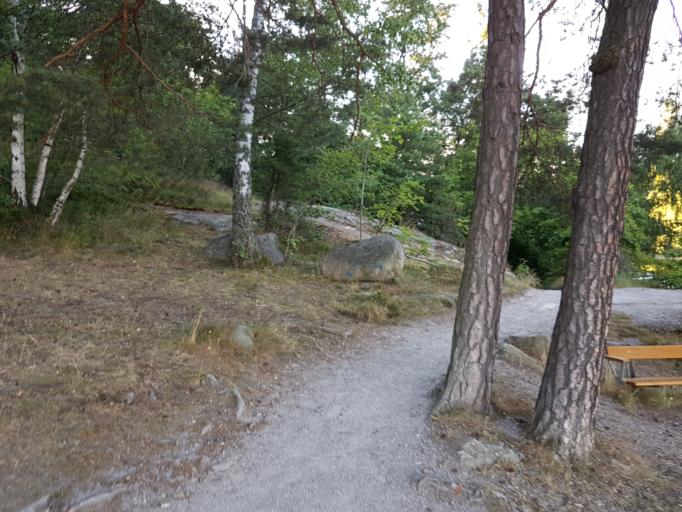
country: SE
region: Stockholm
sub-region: Sundbybergs Kommun
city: Sundbyberg
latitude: 59.3233
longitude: 17.9807
